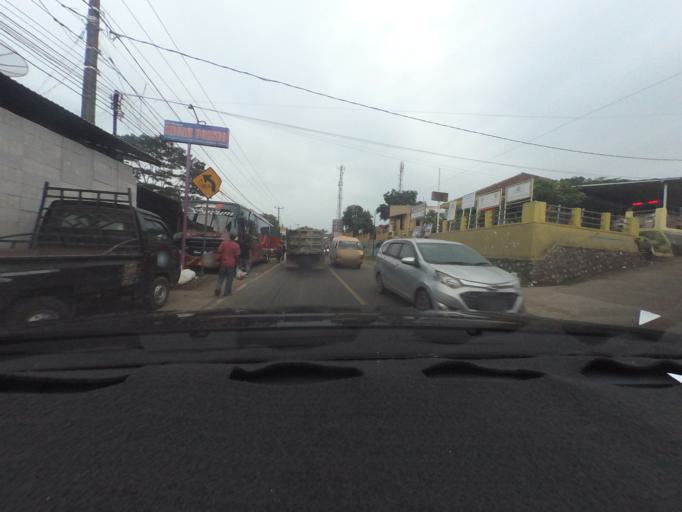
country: ID
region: West Java
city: Cicurug
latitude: -6.8144
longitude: 106.7675
